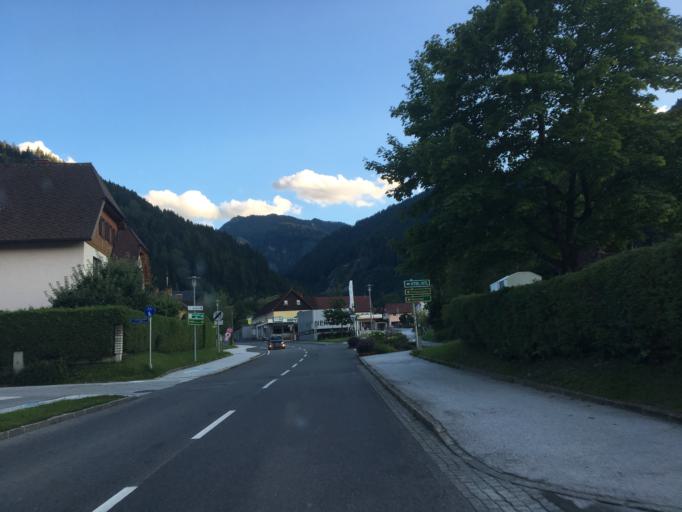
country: AT
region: Styria
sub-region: Politischer Bezirk Liezen
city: Trieben
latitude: 47.4855
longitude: 14.4867
